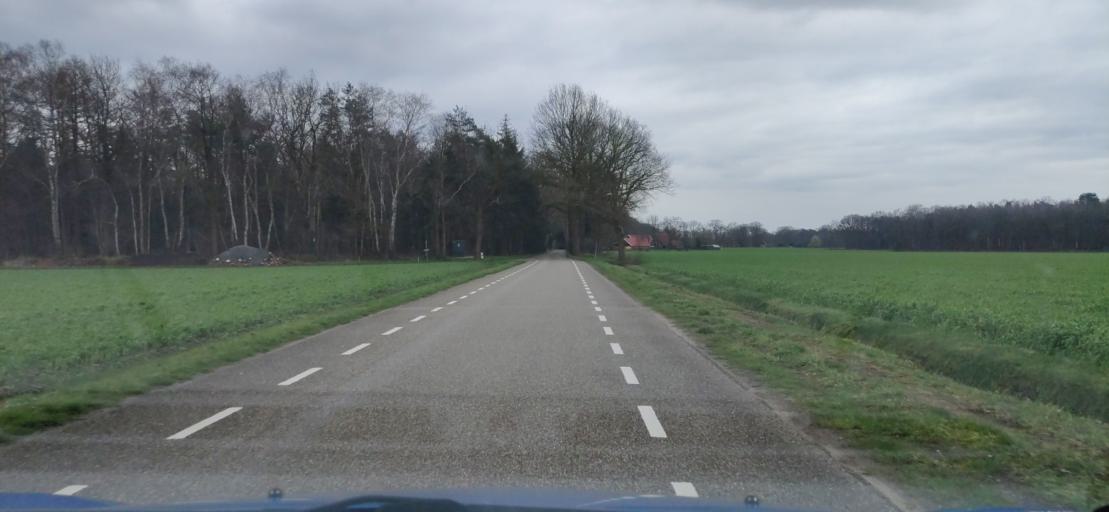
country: NL
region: Overijssel
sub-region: Gemeente Hengelo
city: Hengelo
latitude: 52.2265
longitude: 6.7667
